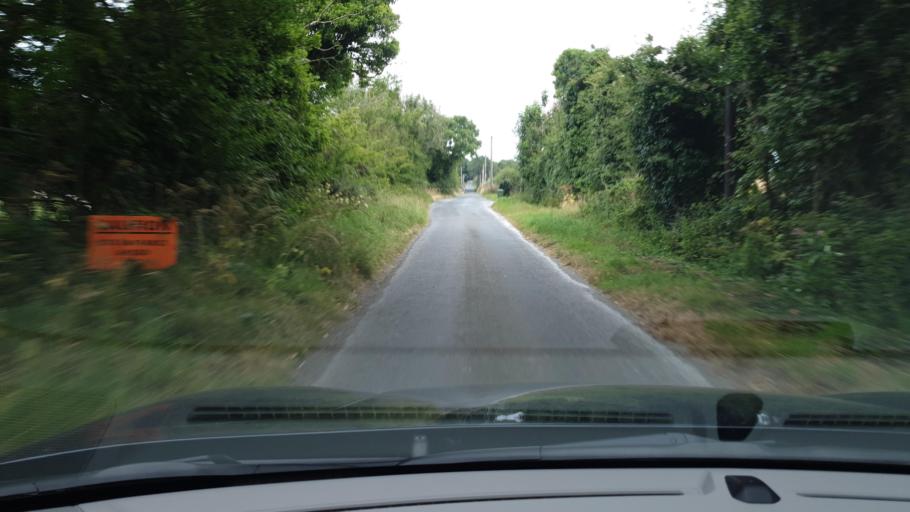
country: IE
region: Leinster
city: Balrothery
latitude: 53.5768
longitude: -6.1786
